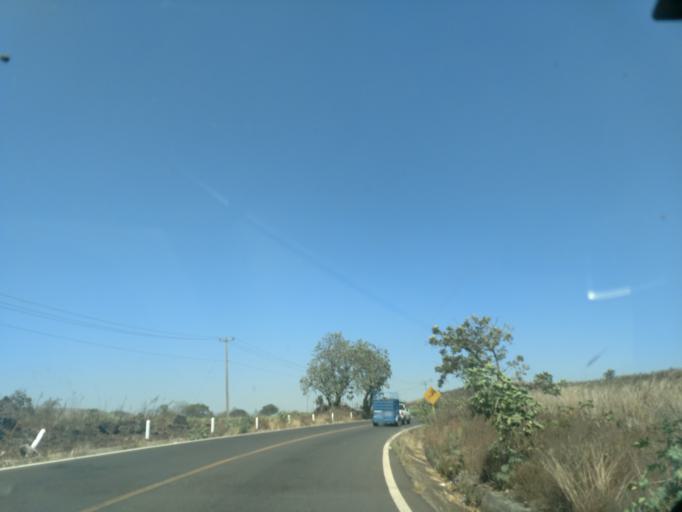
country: MX
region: Nayarit
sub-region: Tepic
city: La Corregidora
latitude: 21.5022
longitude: -104.7559
